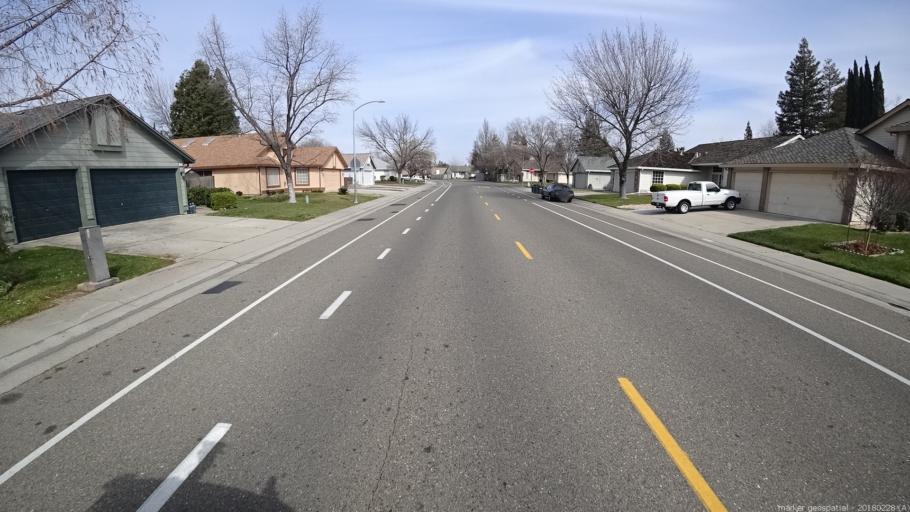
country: US
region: California
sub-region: Sacramento County
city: Antelope
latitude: 38.7198
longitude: -121.3396
